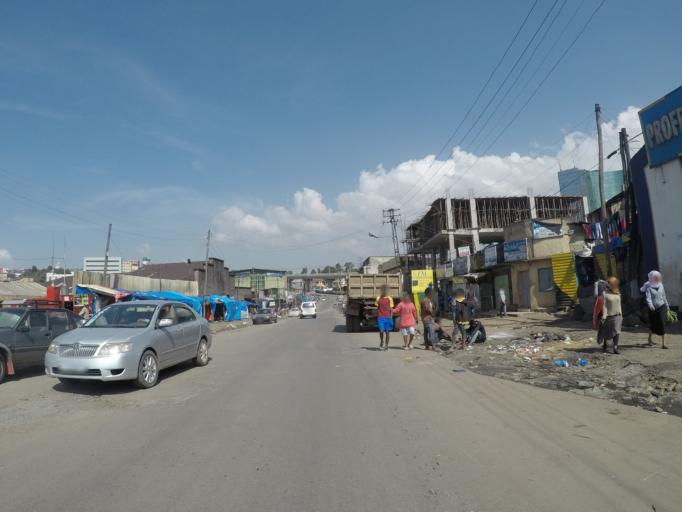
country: ET
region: Adis Abeba
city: Addis Ababa
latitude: 9.0333
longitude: 38.7449
